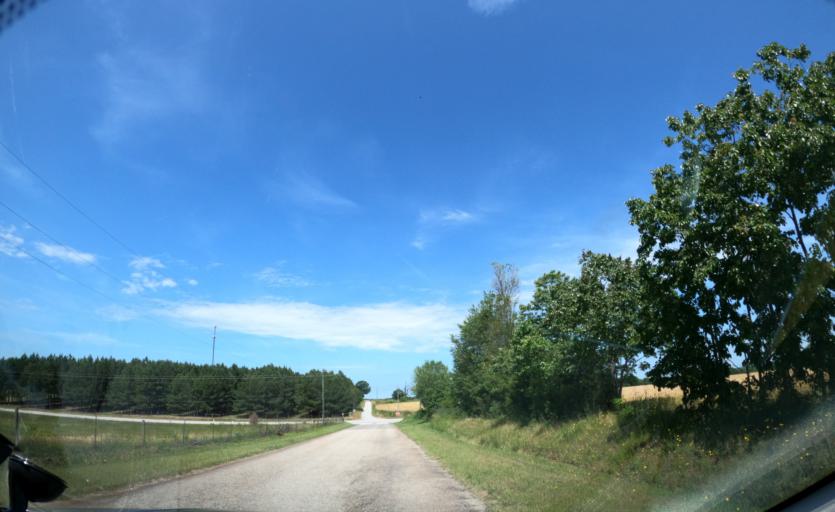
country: US
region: Georgia
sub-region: Elbert County
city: Elberton
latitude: 34.2325
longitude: -82.8958
